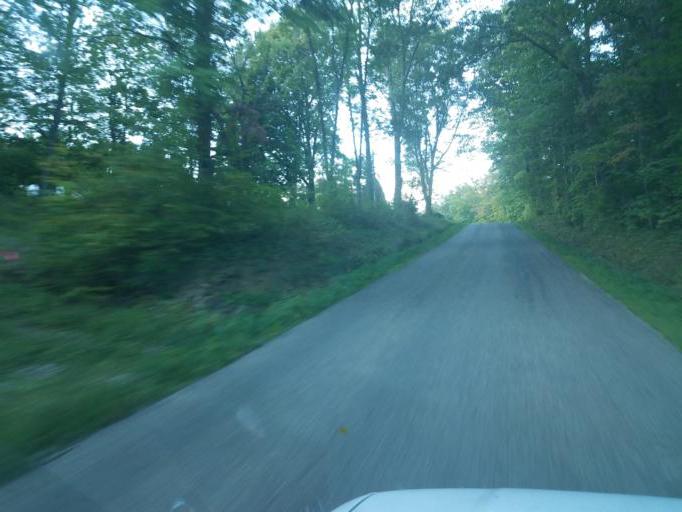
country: US
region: Ohio
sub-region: Knox County
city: Fredericktown
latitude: 40.3983
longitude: -82.5981
